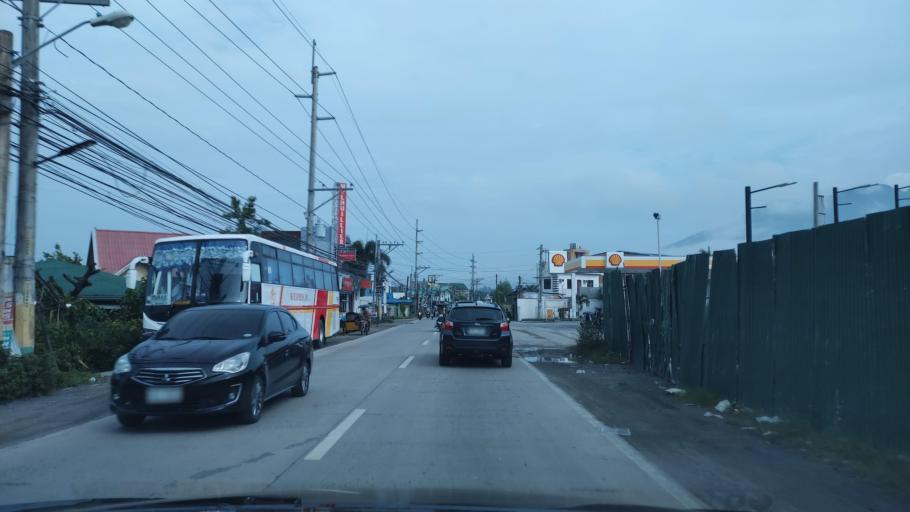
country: PH
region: Central Luzon
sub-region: Province of Pampanga
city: Arayat
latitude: 15.1454
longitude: 120.7686
